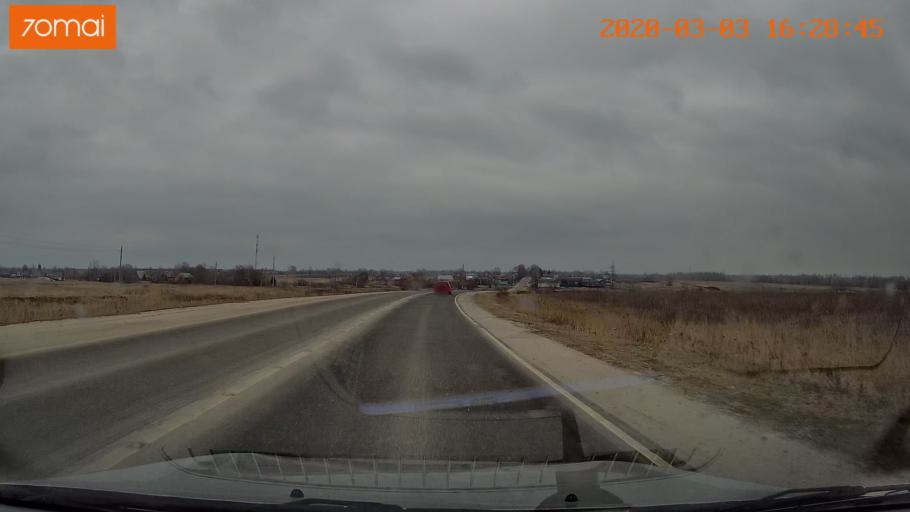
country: RU
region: Moskovskaya
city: Konobeyevo
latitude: 55.4388
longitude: 38.6923
